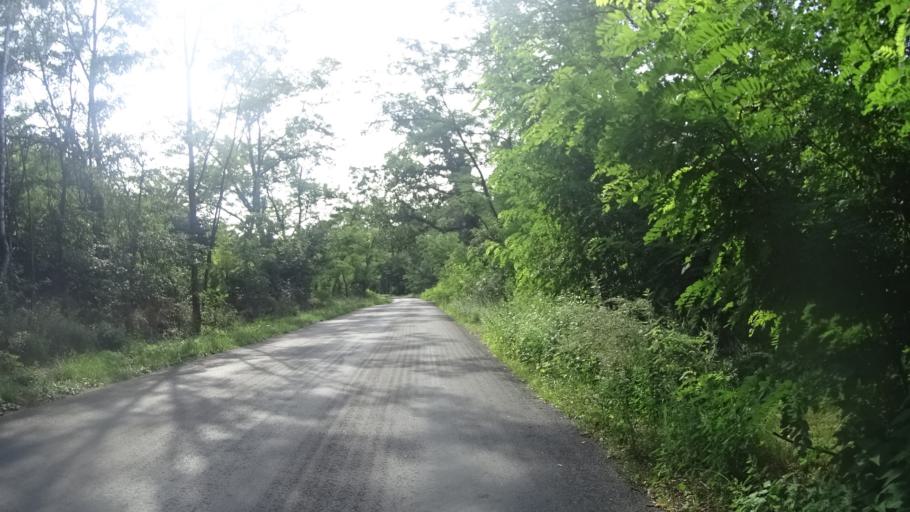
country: DE
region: Brandenburg
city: Golzow
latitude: 52.3265
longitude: 12.6726
